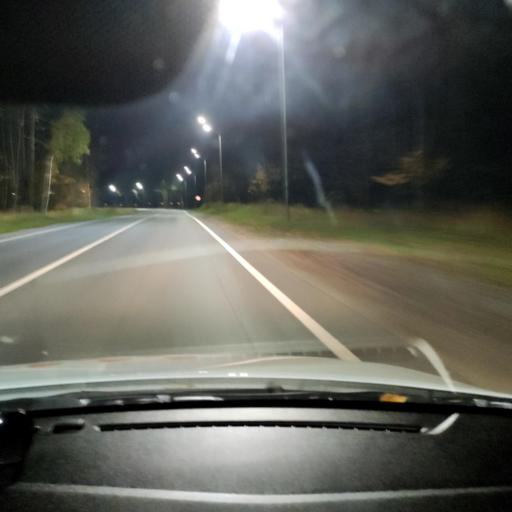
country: RU
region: Tatarstan
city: Stolbishchi
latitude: 55.6334
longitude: 49.0962
